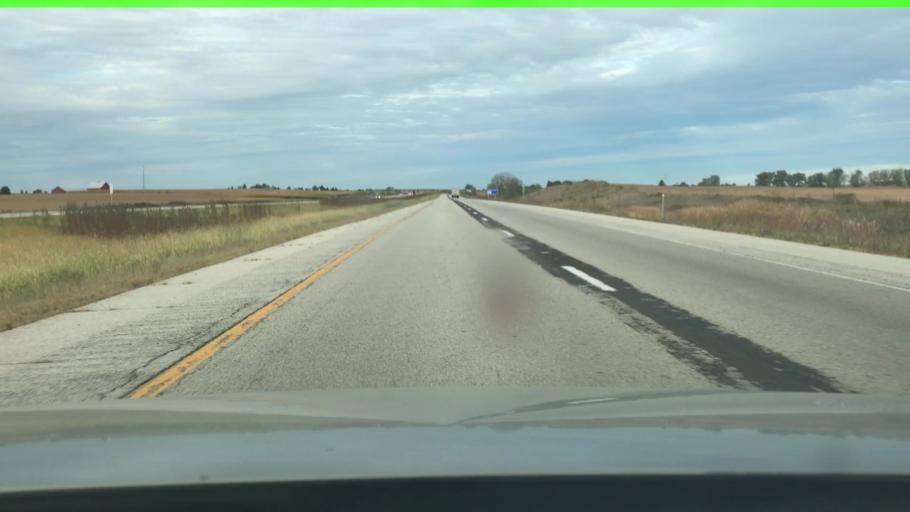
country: US
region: Illinois
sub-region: Livingston County
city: Odell
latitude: 41.0241
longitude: -88.5114
